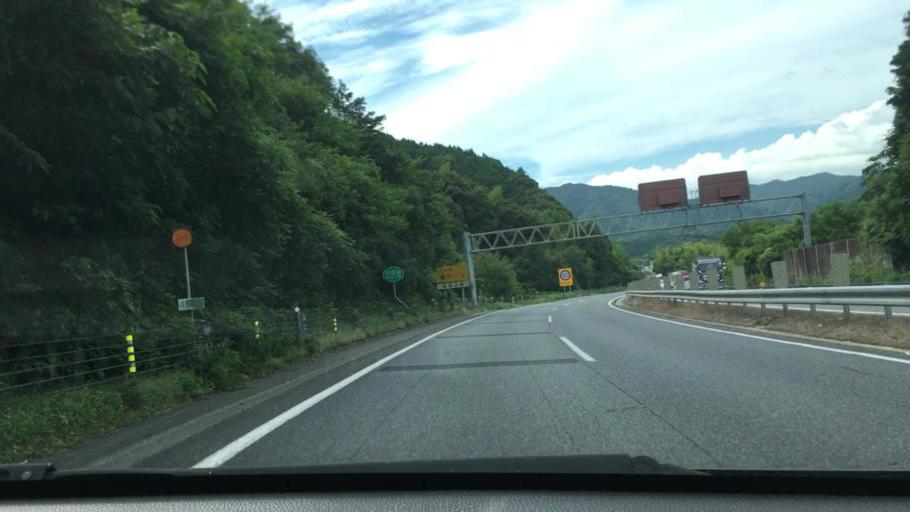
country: JP
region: Yamaguchi
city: Ogori-shimogo
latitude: 34.1299
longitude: 131.4354
